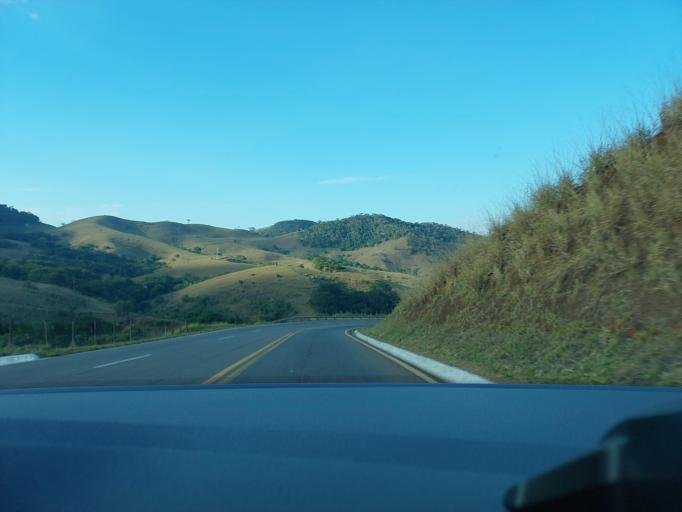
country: BR
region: Minas Gerais
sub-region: Muriae
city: Muriae
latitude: -21.0910
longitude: -42.4781
